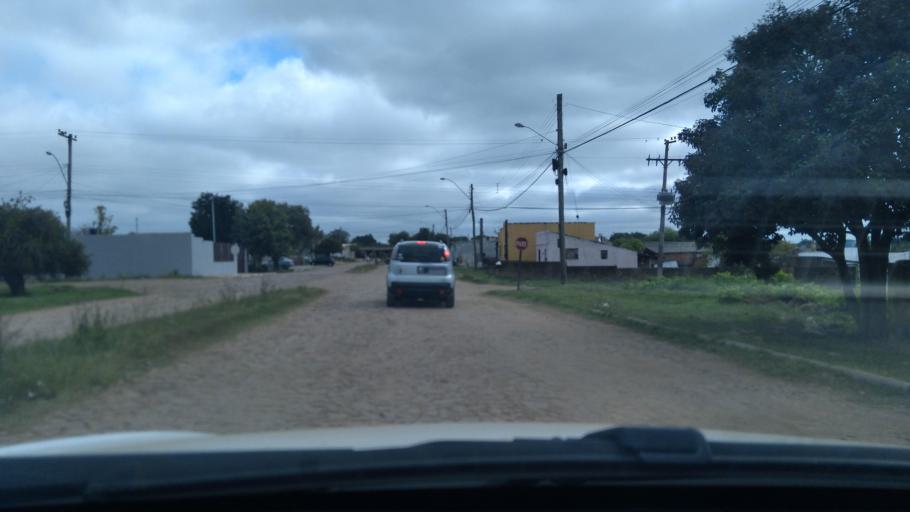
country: BR
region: Rio Grande do Sul
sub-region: Dom Pedrito
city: Dom Pedrito
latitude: -30.9808
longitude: -54.6603
